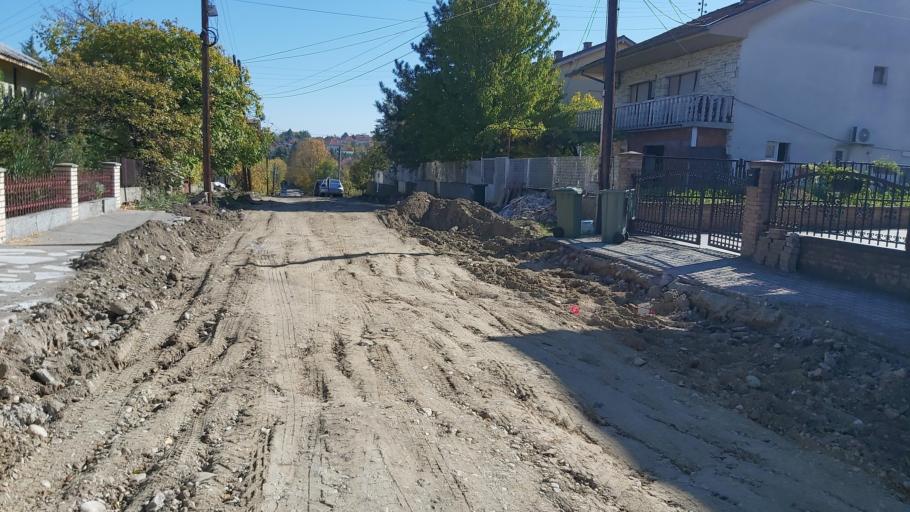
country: MK
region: Negotino
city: Negotino
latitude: 41.4818
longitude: 22.0805
